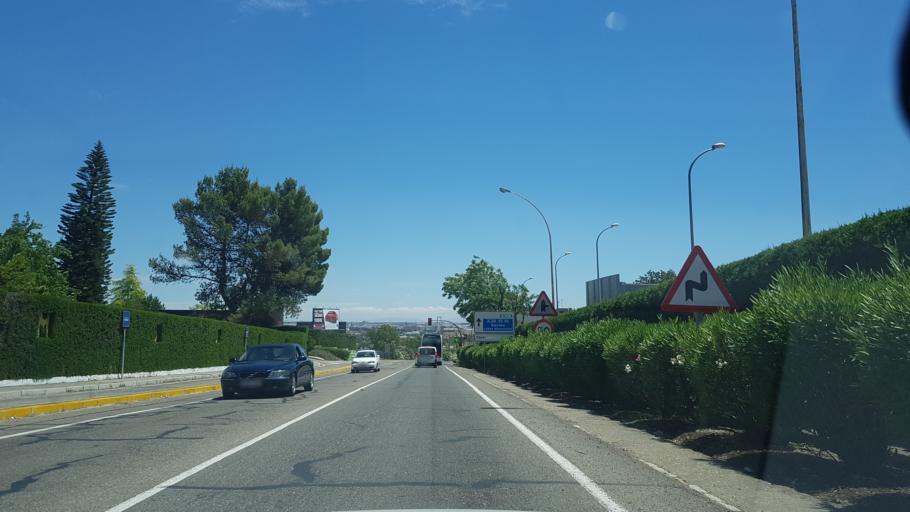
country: ES
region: Andalusia
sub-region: Provincia de Sevilla
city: Castilleja de la Cuesta
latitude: 37.3865
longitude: -6.0380
